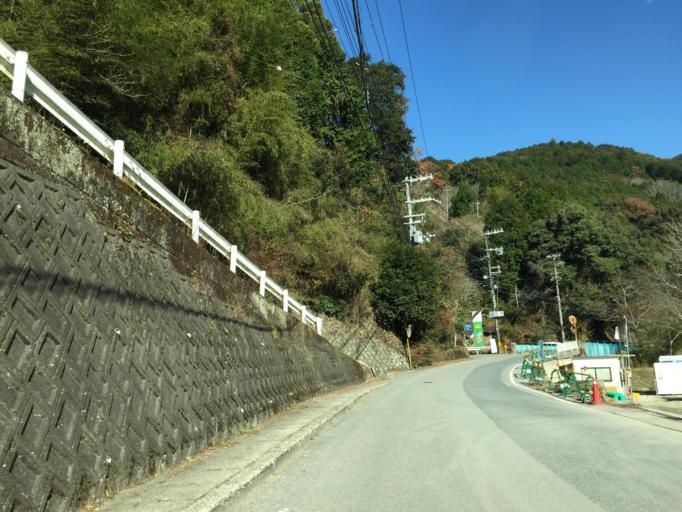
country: JP
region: Wakayama
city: Iwade
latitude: 34.1410
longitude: 135.4177
